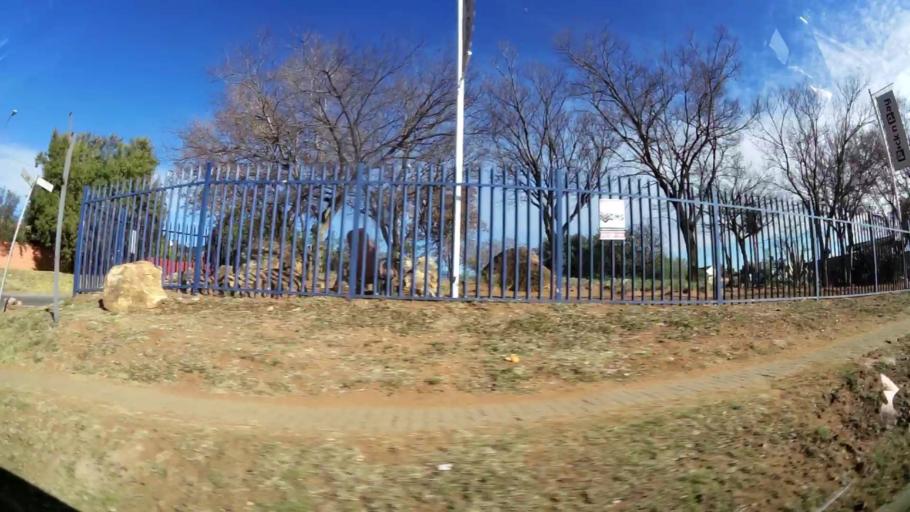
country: ZA
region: Gauteng
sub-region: City of Johannesburg Metropolitan Municipality
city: Roodepoort
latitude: -26.1198
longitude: 27.8505
